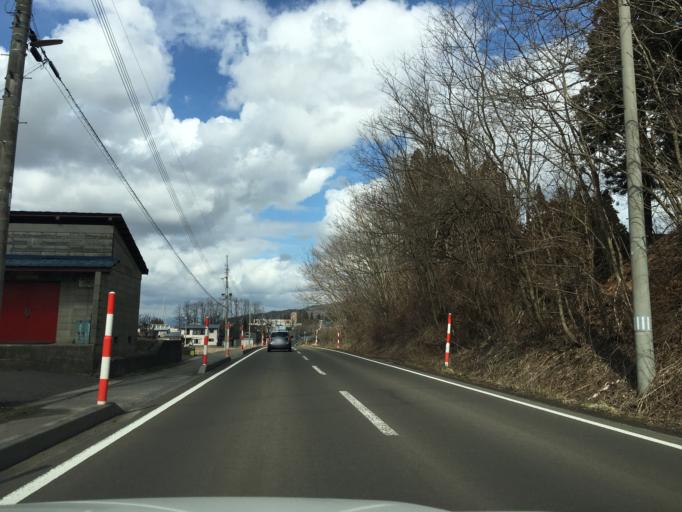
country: JP
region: Akita
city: Odate
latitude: 40.2135
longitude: 140.5834
